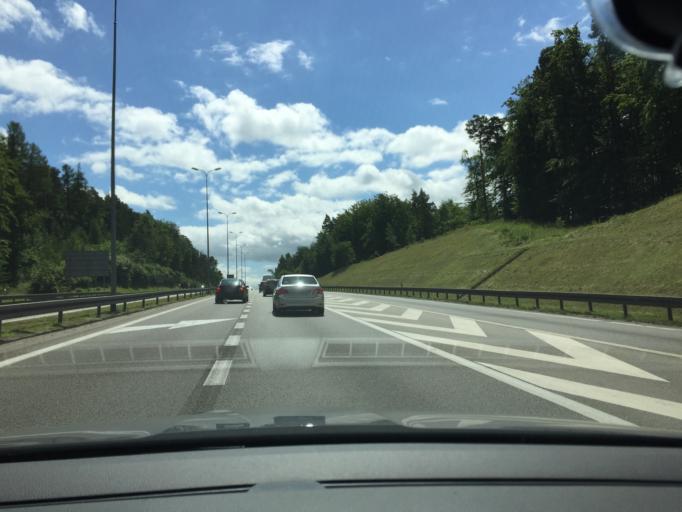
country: PL
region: Pomeranian Voivodeship
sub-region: Gdynia
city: Wielki Kack
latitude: 54.5112
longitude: 18.4574
